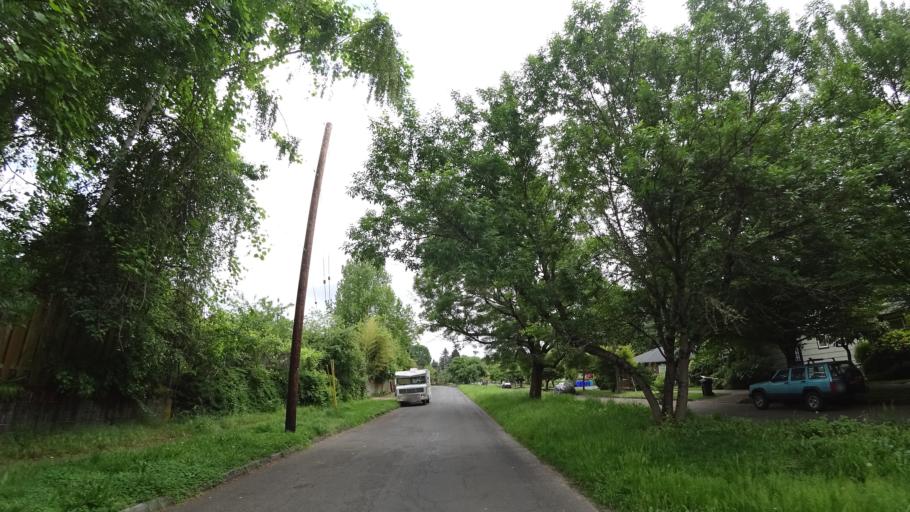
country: US
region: Oregon
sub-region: Multnomah County
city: Portland
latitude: 45.4986
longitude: -122.6304
